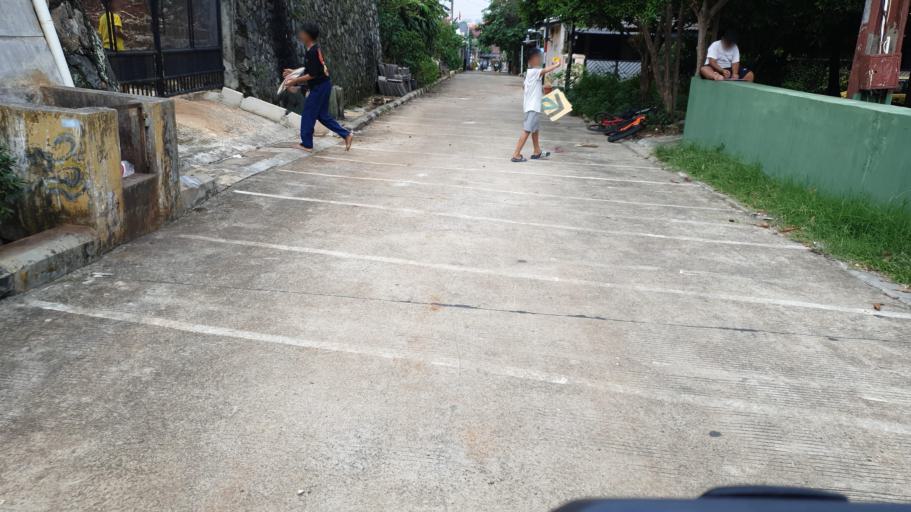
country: ID
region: West Java
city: Depok
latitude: -6.3702
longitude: 106.8528
